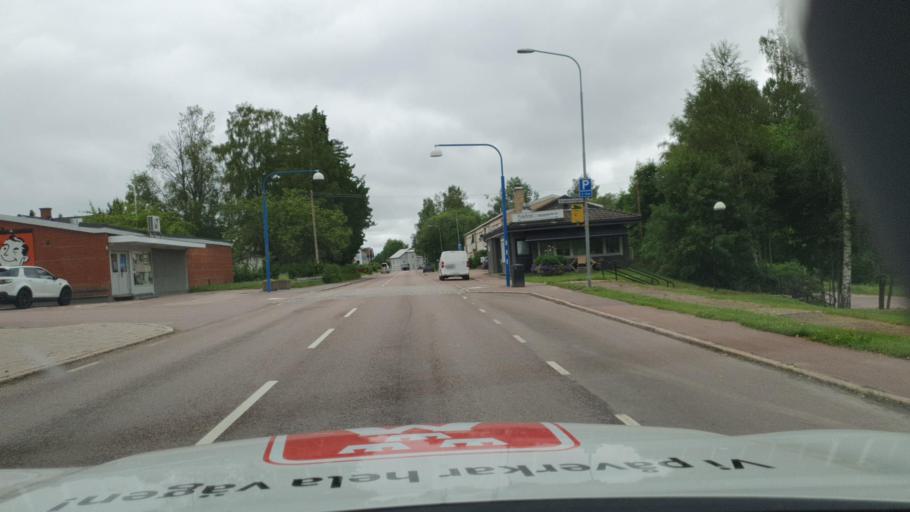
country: SE
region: Vaermland
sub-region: Karlstads Kommun
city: Edsvalla
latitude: 59.4354
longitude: 13.2111
